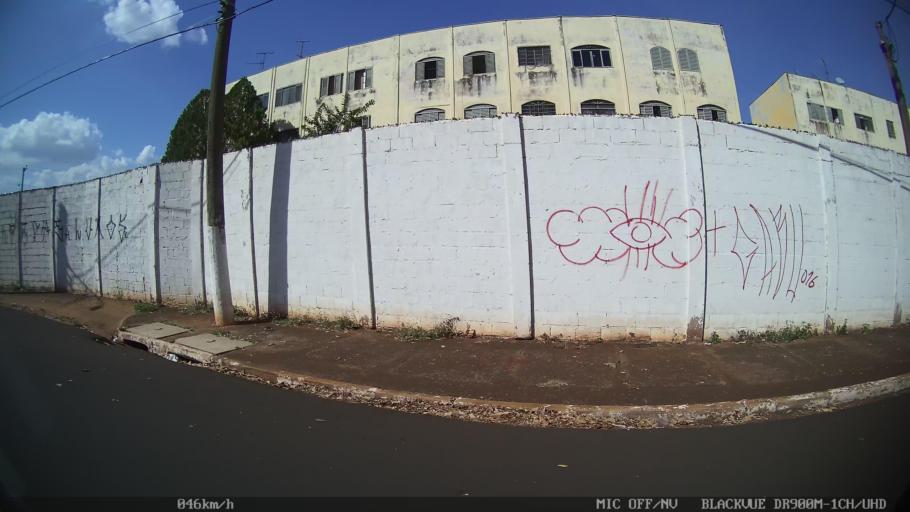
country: BR
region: Sao Paulo
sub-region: Ribeirao Preto
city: Ribeirao Preto
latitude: -21.1887
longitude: -47.8257
